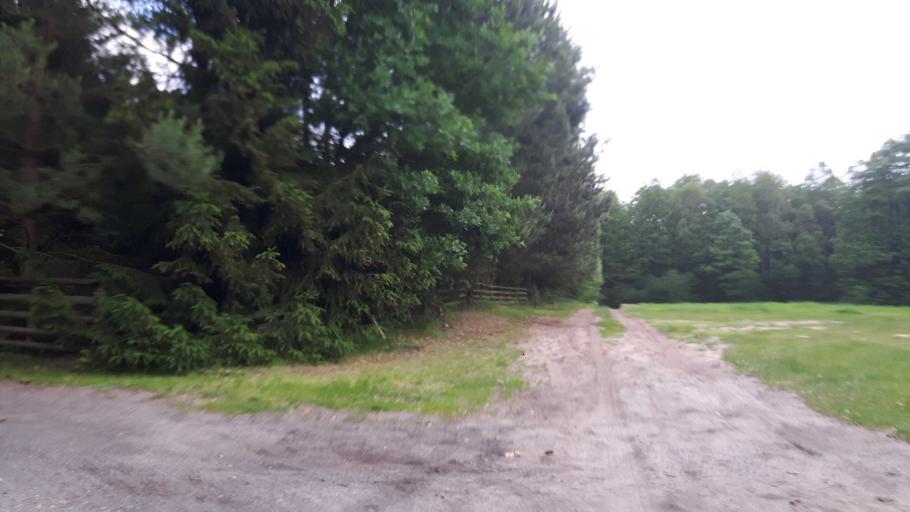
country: PL
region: West Pomeranian Voivodeship
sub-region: Powiat goleniowski
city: Goleniow
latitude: 53.6553
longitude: 14.9034
